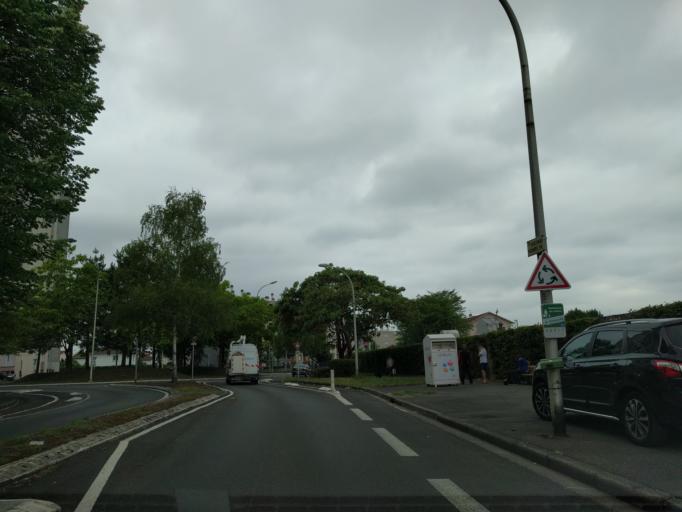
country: FR
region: Midi-Pyrenees
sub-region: Departement des Hautes-Pyrenees
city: Tarbes
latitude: 43.2331
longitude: 0.0619
